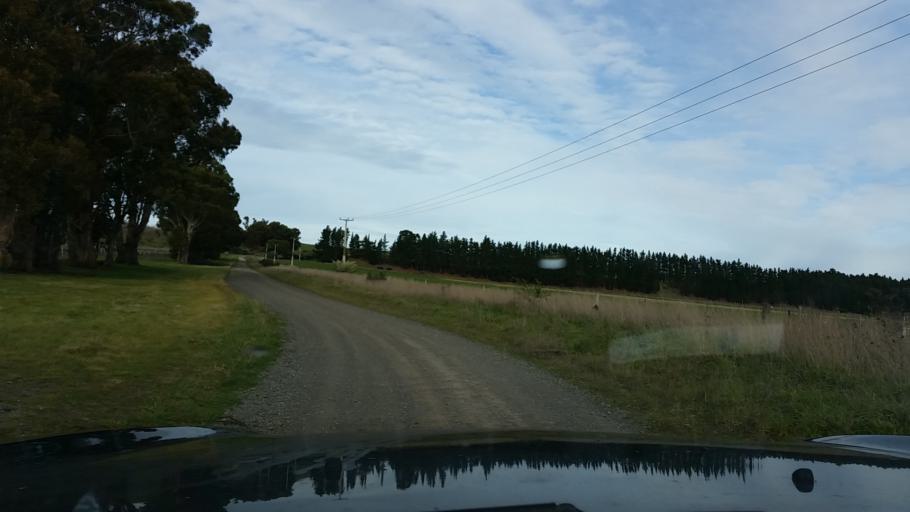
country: NZ
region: Marlborough
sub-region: Marlborough District
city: Blenheim
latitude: -41.6347
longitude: 174.1199
